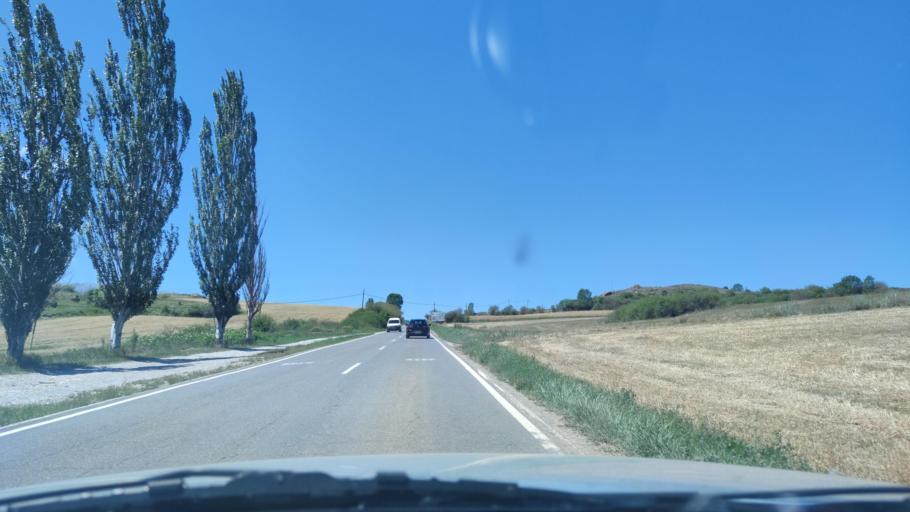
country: ES
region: Catalonia
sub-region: Provincia de Girona
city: Isovol
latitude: 42.3647
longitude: 1.8250
